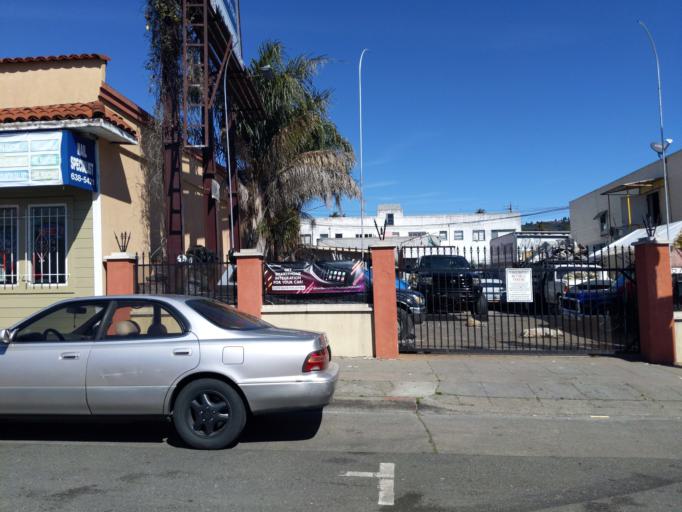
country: US
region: California
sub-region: Alameda County
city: San Leandro
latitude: 37.7696
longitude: -122.1814
